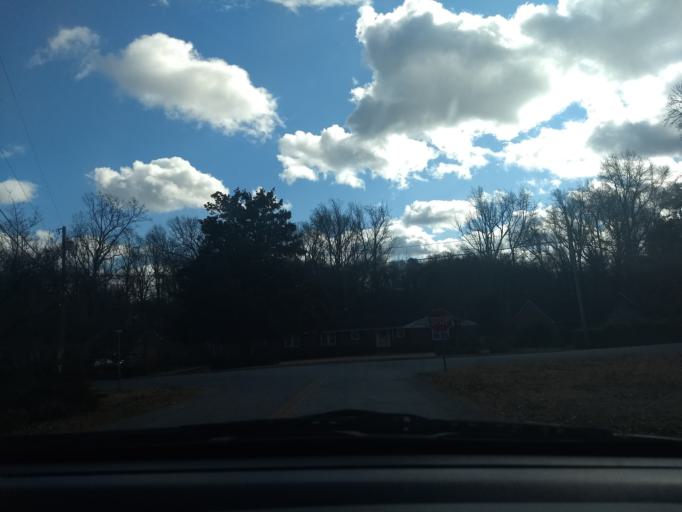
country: US
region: South Carolina
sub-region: Greenville County
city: Wade Hampton
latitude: 34.8760
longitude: -82.3545
